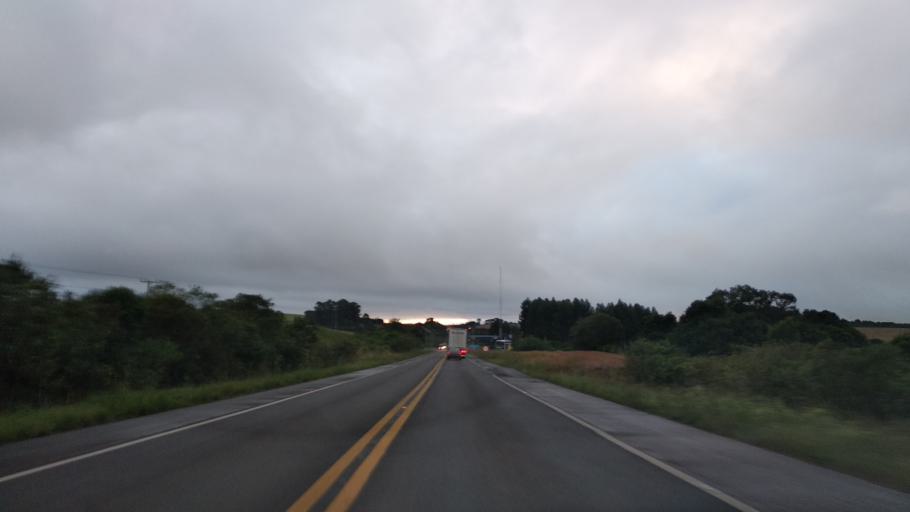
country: BR
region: Santa Catarina
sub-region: Campos Novos
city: Campos Novos
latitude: -27.3886
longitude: -51.1178
